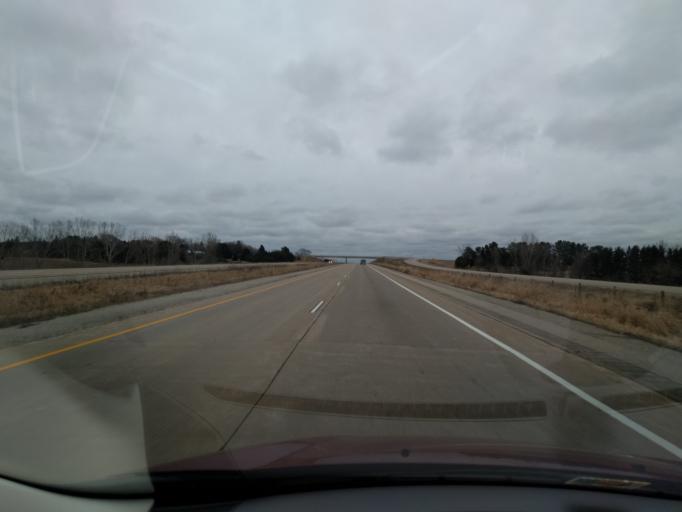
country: US
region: Wisconsin
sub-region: Winnebago County
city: Winneconne
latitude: 44.1880
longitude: -88.6699
